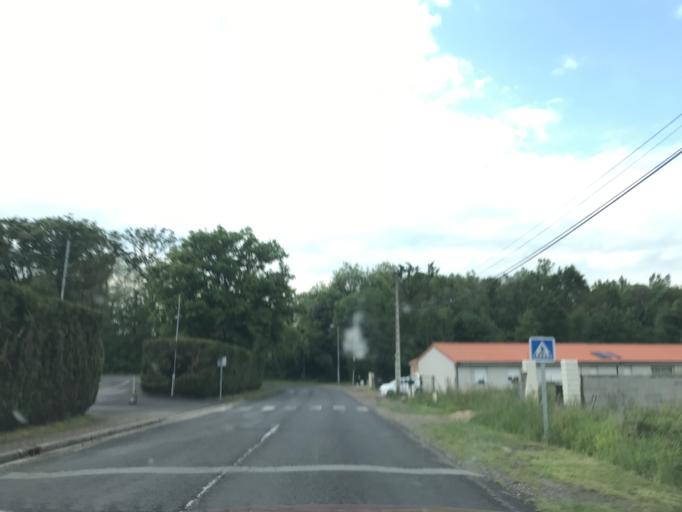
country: FR
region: Auvergne
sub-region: Departement du Puy-de-Dome
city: Orleat
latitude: 45.8919
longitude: 3.3880
